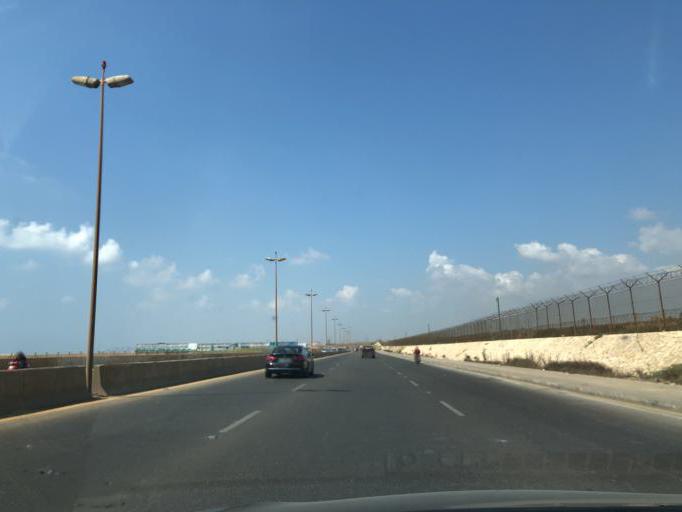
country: LB
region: Mont-Liban
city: Baabda
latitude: 33.8010
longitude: 35.4796
